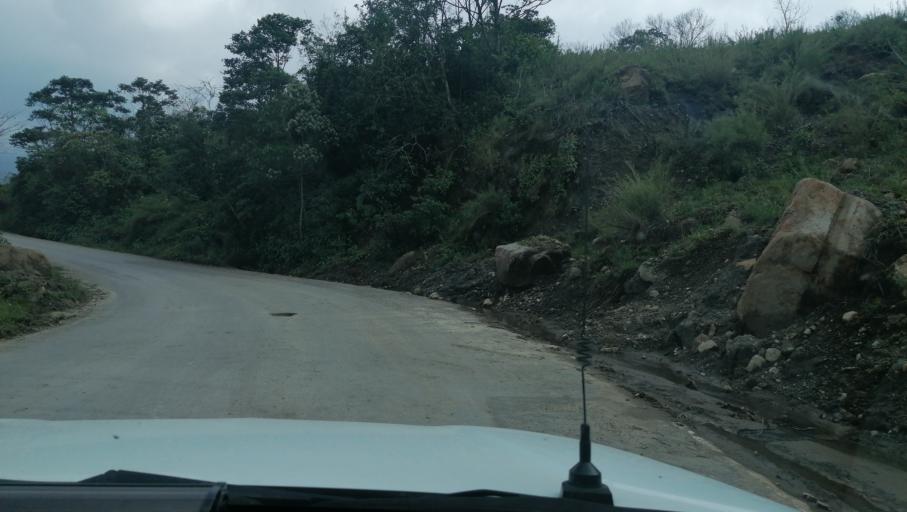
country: MX
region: Chiapas
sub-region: Ocotepec
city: San Pablo Huacano
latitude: 17.2585
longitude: -93.2674
